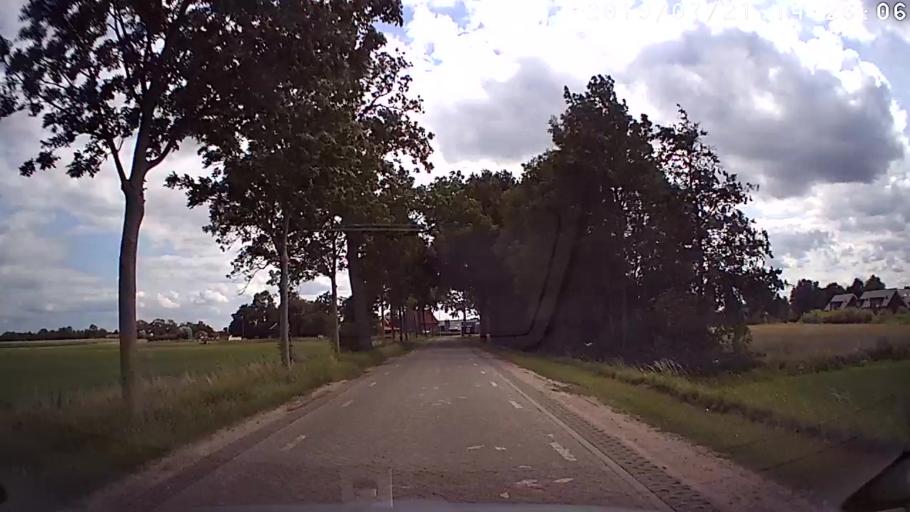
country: NL
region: Overijssel
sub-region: Gemeente Raalte
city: Heino
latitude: 52.4397
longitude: 6.1911
